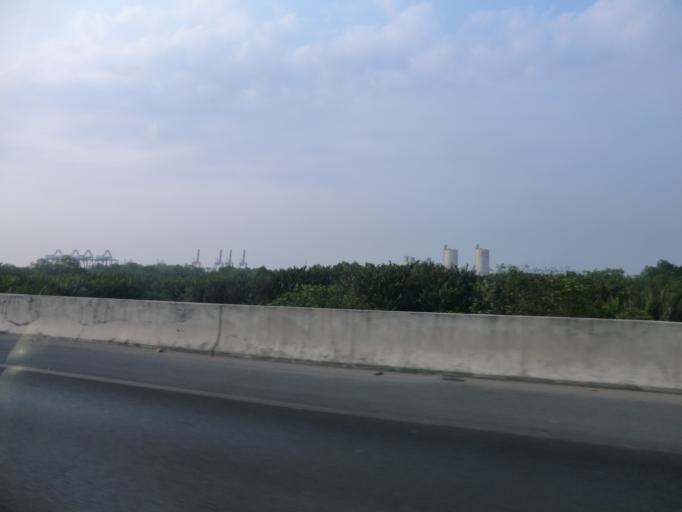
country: VN
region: Ho Chi Minh City
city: Quan Chin
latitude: 10.7927
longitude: 106.8123
